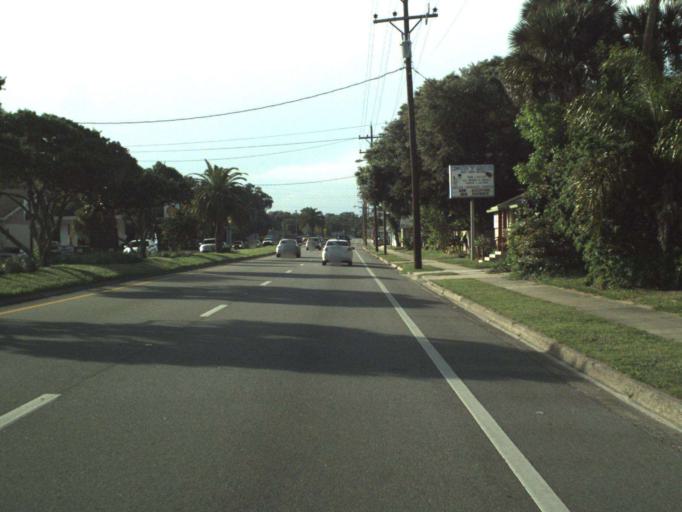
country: US
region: Florida
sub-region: Volusia County
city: New Smyrna Beach
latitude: 29.0368
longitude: -80.9319
